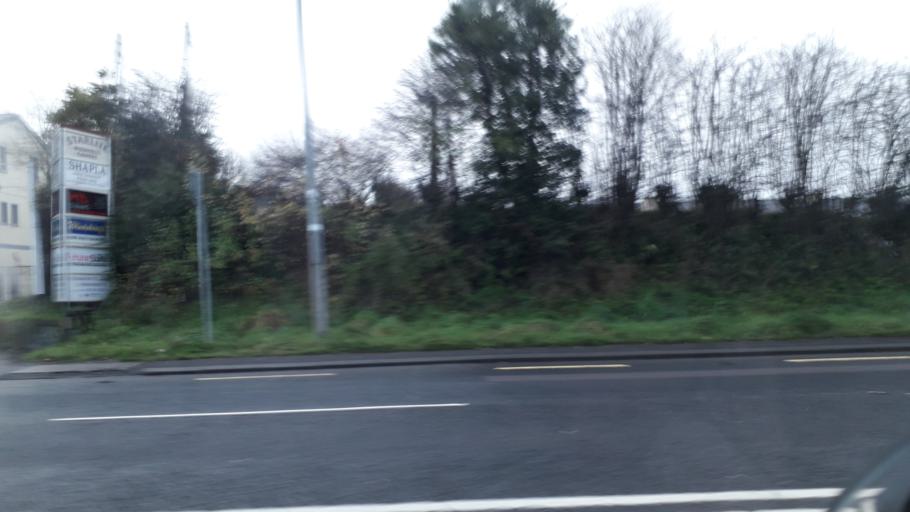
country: IE
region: Ulster
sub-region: County Donegal
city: Letterkenny
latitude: 54.9471
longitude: -7.7104
